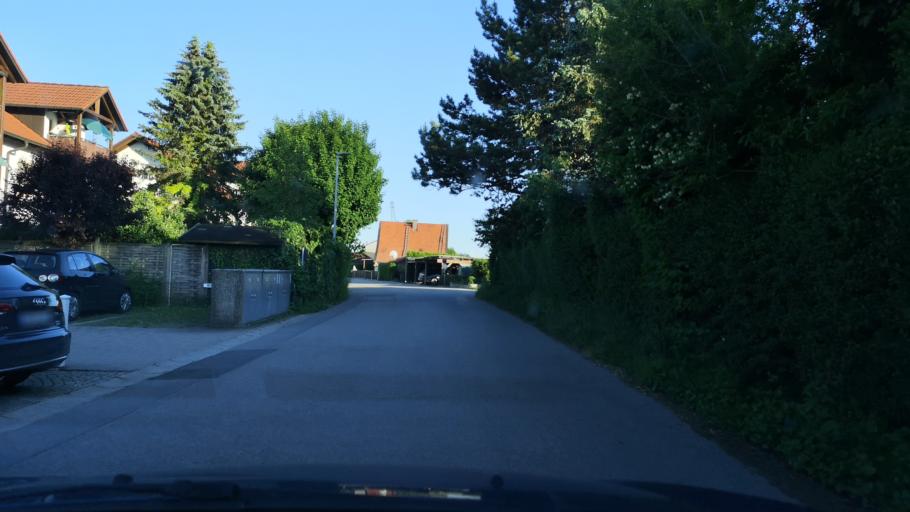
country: DE
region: Bavaria
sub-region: Upper Bavaria
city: Kirchheim bei Muenchen
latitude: 48.1963
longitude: 11.7717
